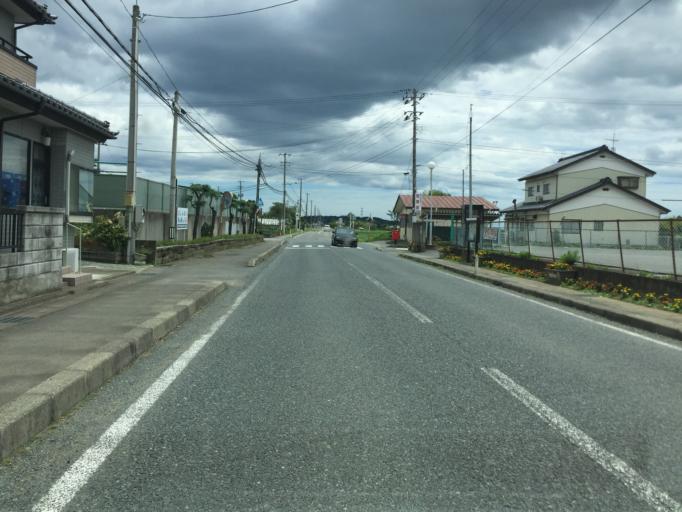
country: JP
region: Fukushima
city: Namie
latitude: 37.6508
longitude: 140.9881
